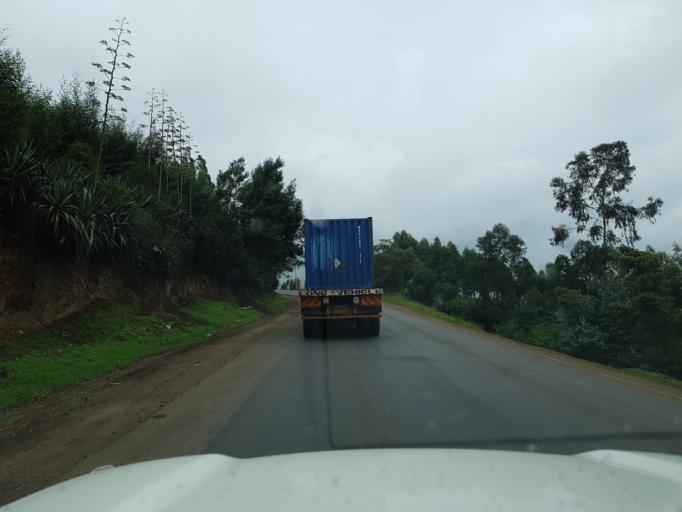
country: KE
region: Kiambu
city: Limuru
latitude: -1.1292
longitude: 36.6299
